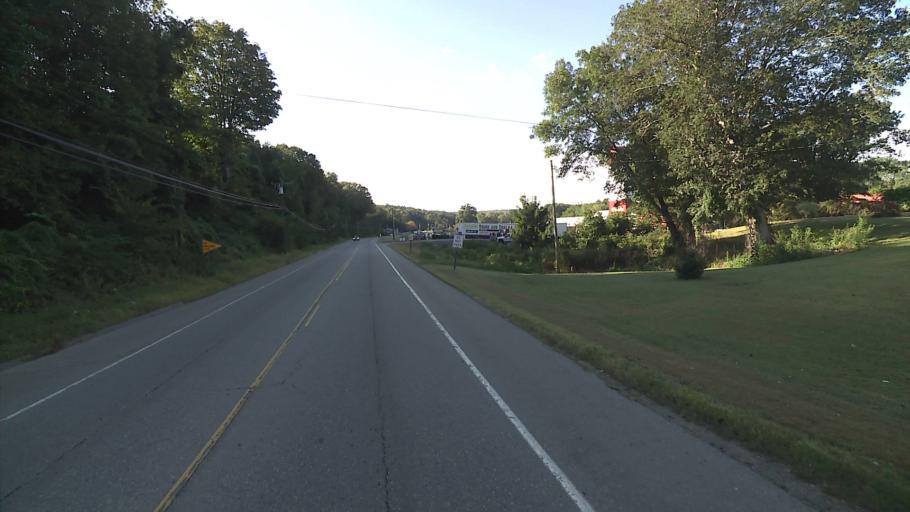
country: US
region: Connecticut
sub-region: New London County
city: Baltic
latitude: 41.5805
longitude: -72.1325
